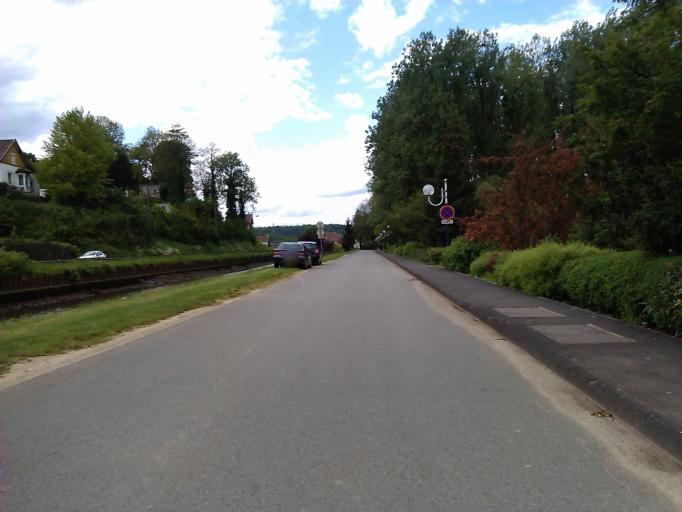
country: FR
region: Franche-Comte
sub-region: Departement du Doubs
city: Arbouans
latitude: 47.5050
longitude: 6.8019
